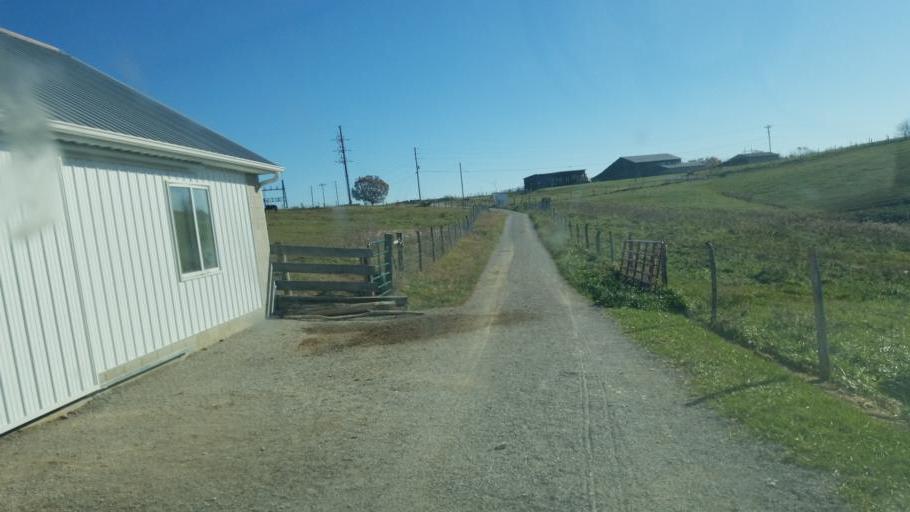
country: US
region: Kentucky
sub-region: Fleming County
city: Flemingsburg
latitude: 38.4668
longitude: -83.5172
